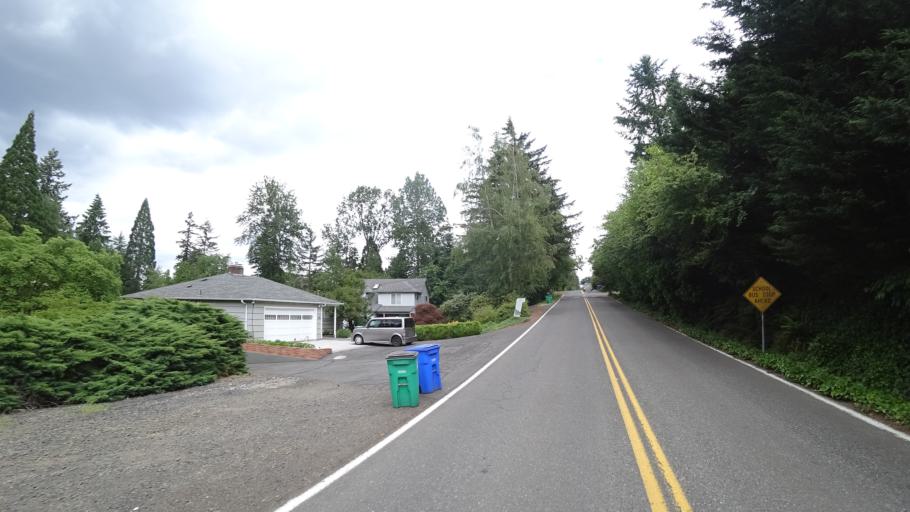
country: US
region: Oregon
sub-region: Clackamas County
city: Lake Oswego
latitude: 45.4518
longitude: -122.7085
